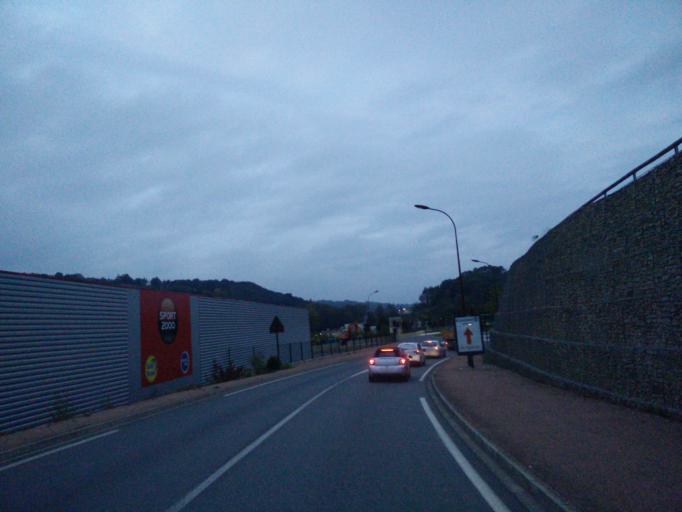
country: FR
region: Aquitaine
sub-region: Departement de la Dordogne
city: Sarlat-la-Caneda
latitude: 44.8774
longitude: 1.2123
